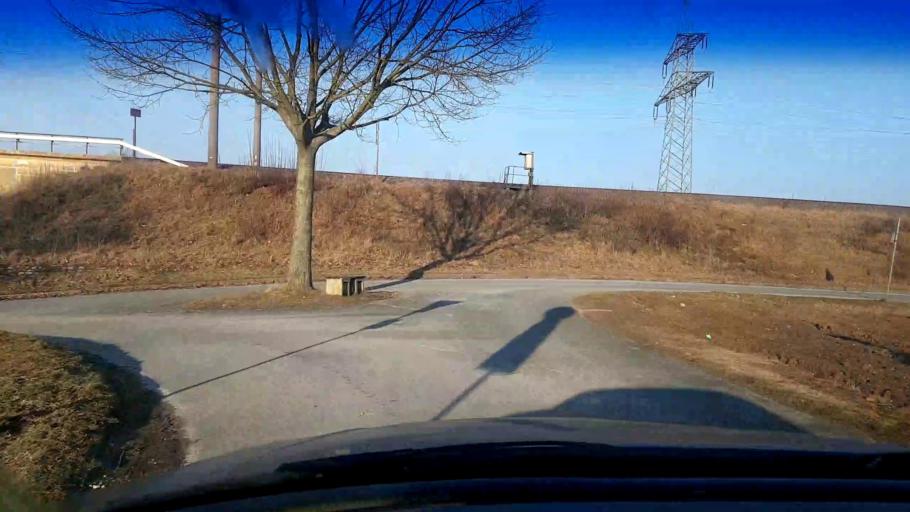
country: DE
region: Bavaria
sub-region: Upper Franconia
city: Hallstadt
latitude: 49.9240
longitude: 10.8631
